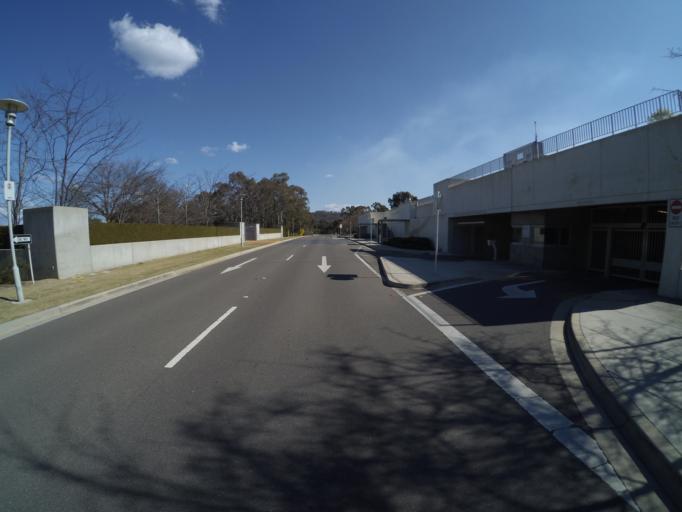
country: AU
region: Australian Capital Territory
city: Forrest
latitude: -35.3086
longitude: 149.1266
